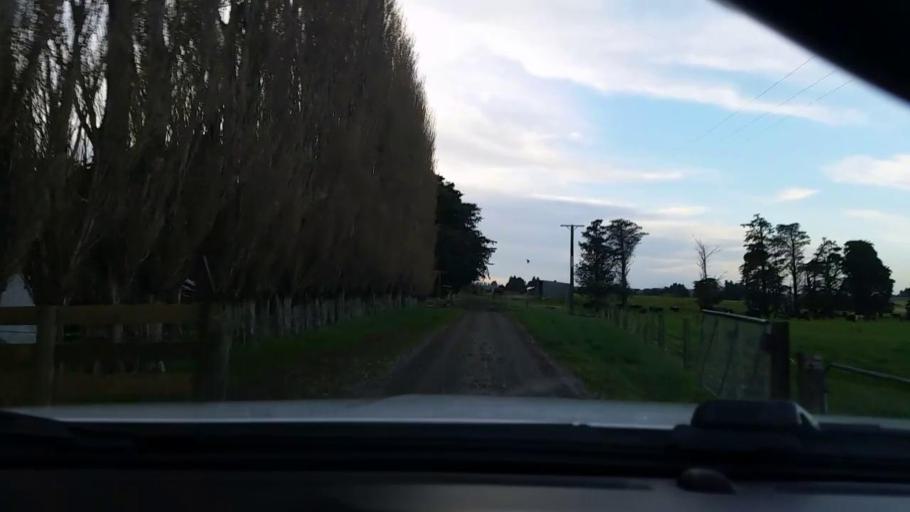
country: NZ
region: Southland
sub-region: Southland District
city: Winton
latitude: -46.1145
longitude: 168.4414
